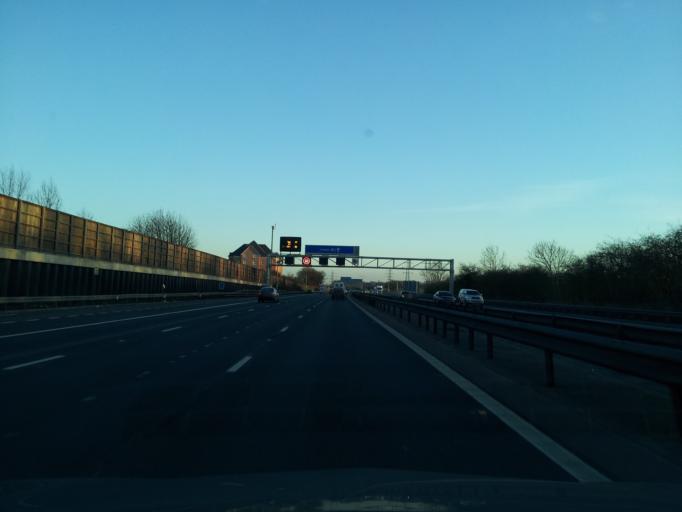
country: GB
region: England
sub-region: Central Bedfordshire
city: Caddington
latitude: 51.8694
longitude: -0.4393
